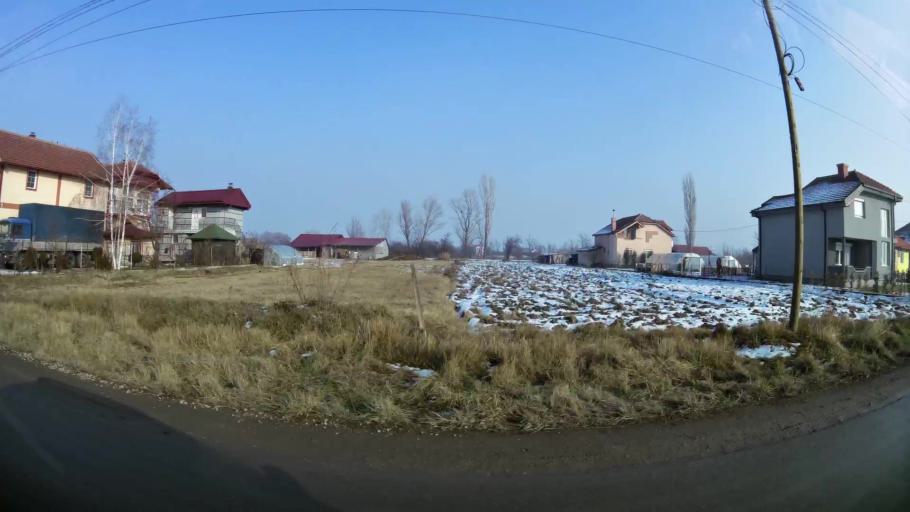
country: MK
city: Kadino
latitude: 41.9595
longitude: 21.6015
